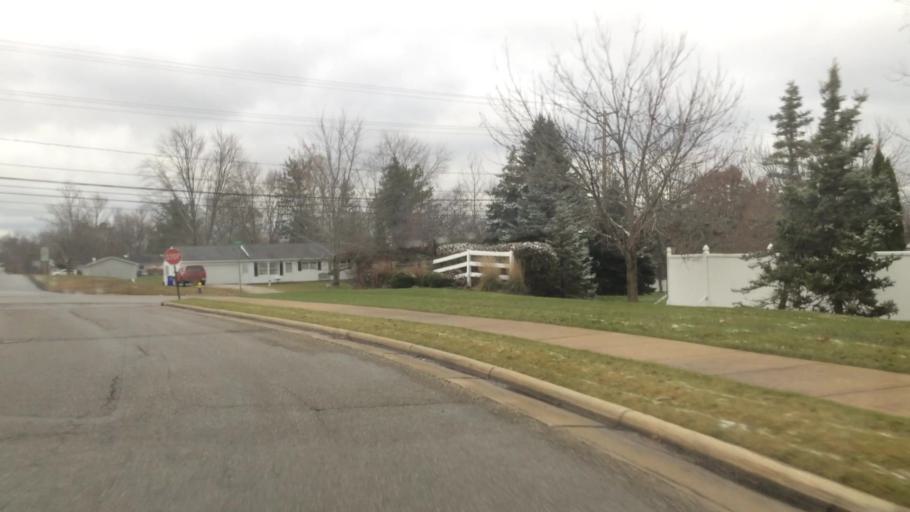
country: US
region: Ohio
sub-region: Portage County
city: Streetsboro
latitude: 41.2622
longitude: -81.3698
